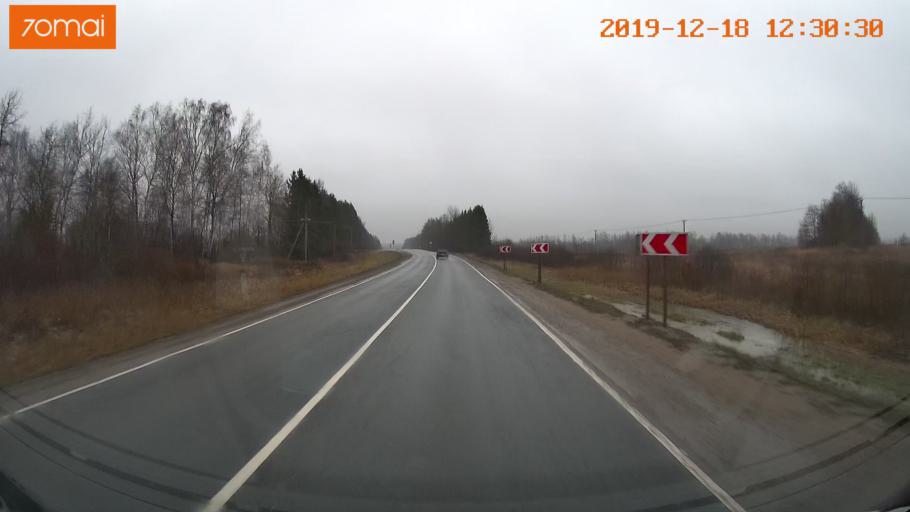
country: RU
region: Moskovskaya
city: Novopetrovskoye
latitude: 56.0899
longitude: 36.5329
